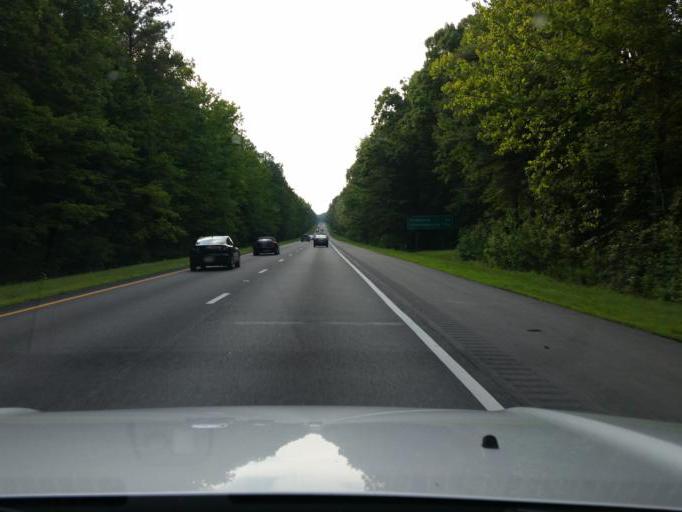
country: US
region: Virginia
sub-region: King William County
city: West Point
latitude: 37.4301
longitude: -76.8405
